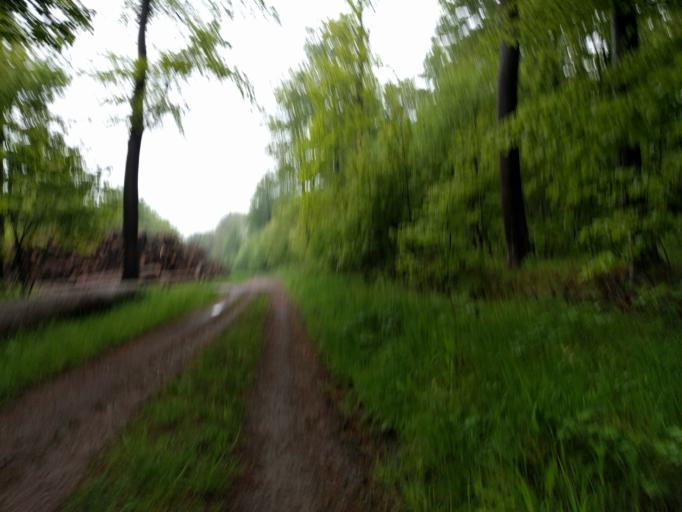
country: DK
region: South Denmark
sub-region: Kerteminde Kommune
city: Munkebo
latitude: 55.4310
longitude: 10.5543
